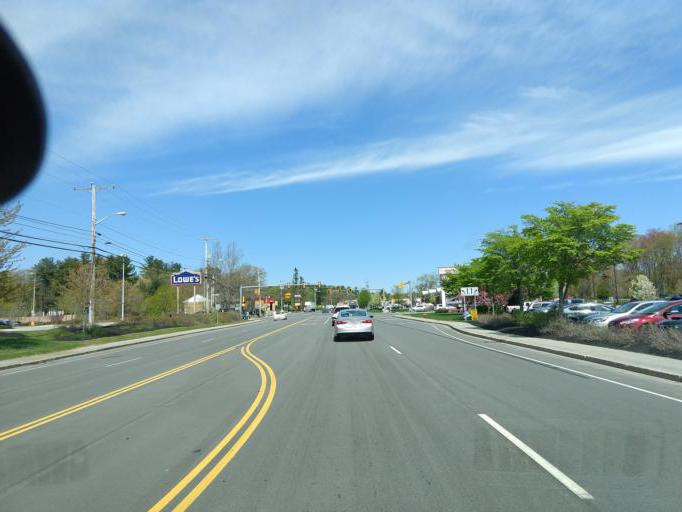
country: US
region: New Hampshire
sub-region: Rockingham County
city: Seabrook
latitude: 42.8858
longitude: -70.8697
